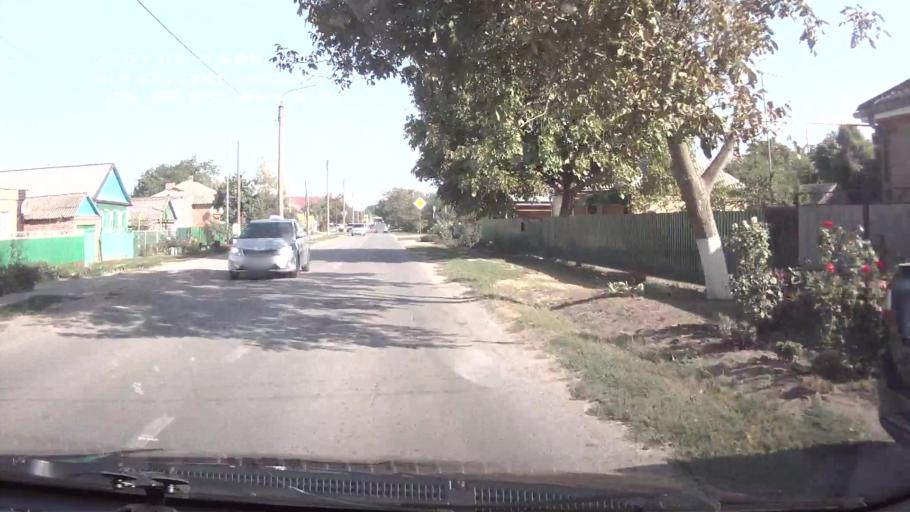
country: RU
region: Rostov
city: Tselina
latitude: 46.5324
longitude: 41.0263
